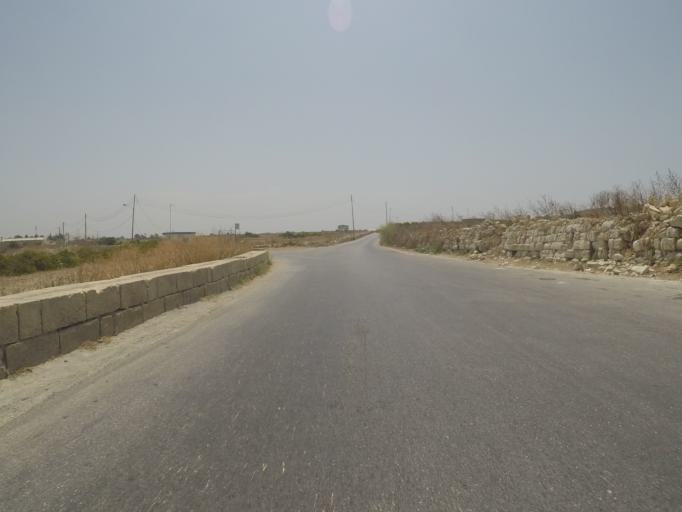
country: MT
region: L-Imdina
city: Imdina
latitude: 35.8776
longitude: 14.4124
